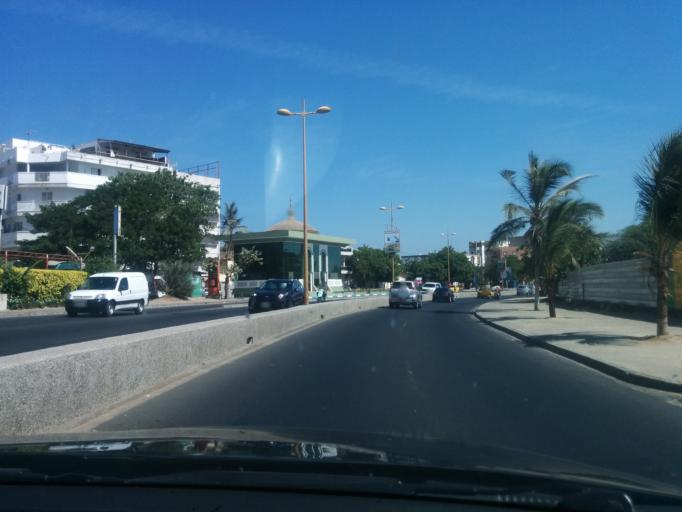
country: SN
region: Dakar
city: Dakar
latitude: 14.6791
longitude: -17.4621
